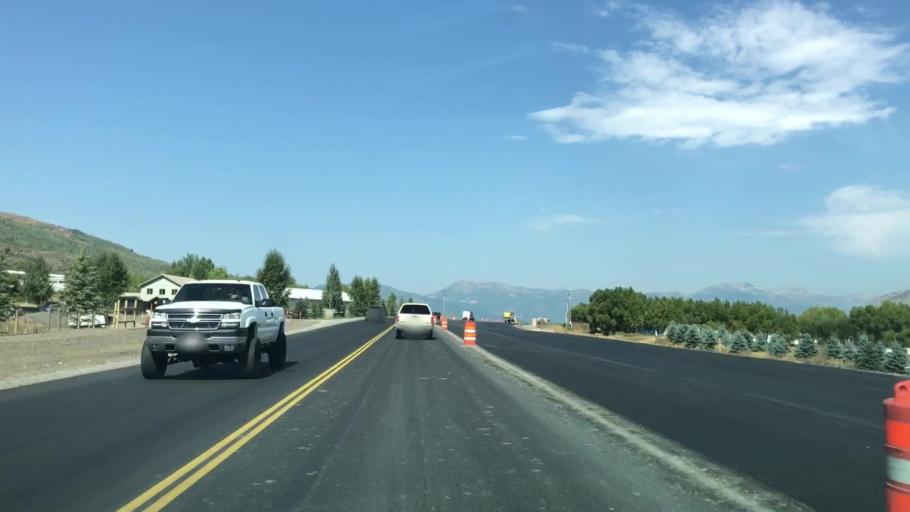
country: US
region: Wyoming
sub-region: Teton County
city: South Park
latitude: 43.3712
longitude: -110.7409
